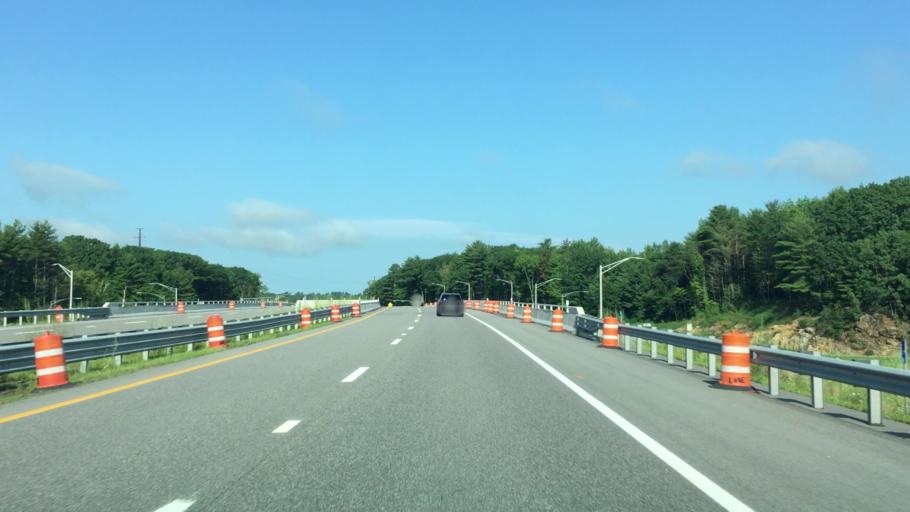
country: US
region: Maine
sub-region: Androscoggin County
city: Lewiston
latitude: 44.0721
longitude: -70.1833
